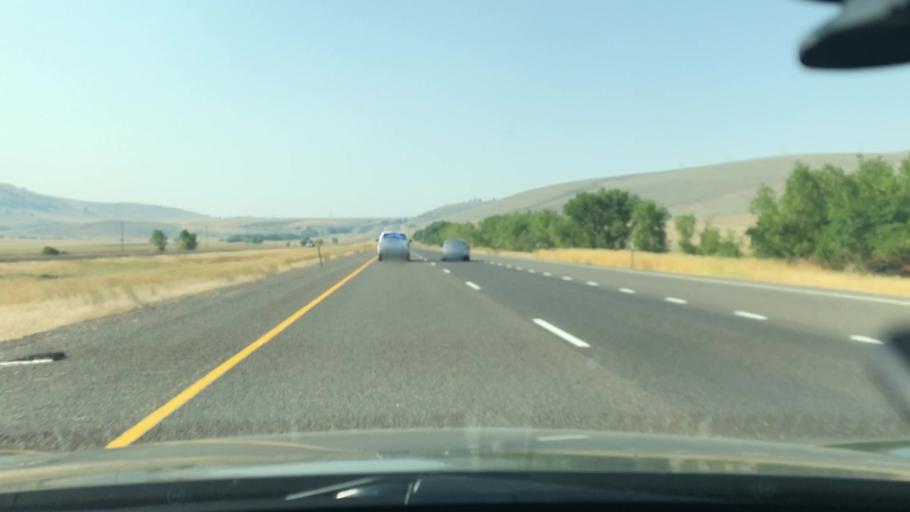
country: US
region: Oregon
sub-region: Union County
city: Union
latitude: 45.1280
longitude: -117.9639
